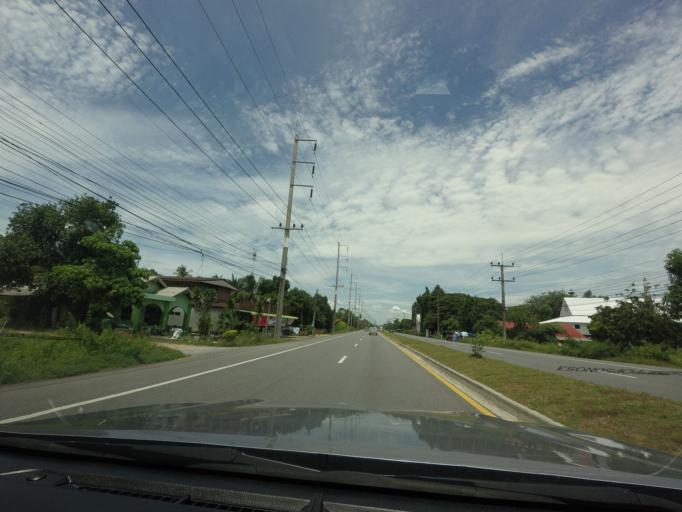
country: TH
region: Songkhla
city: Krasae Sin
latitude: 7.5877
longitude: 100.4051
